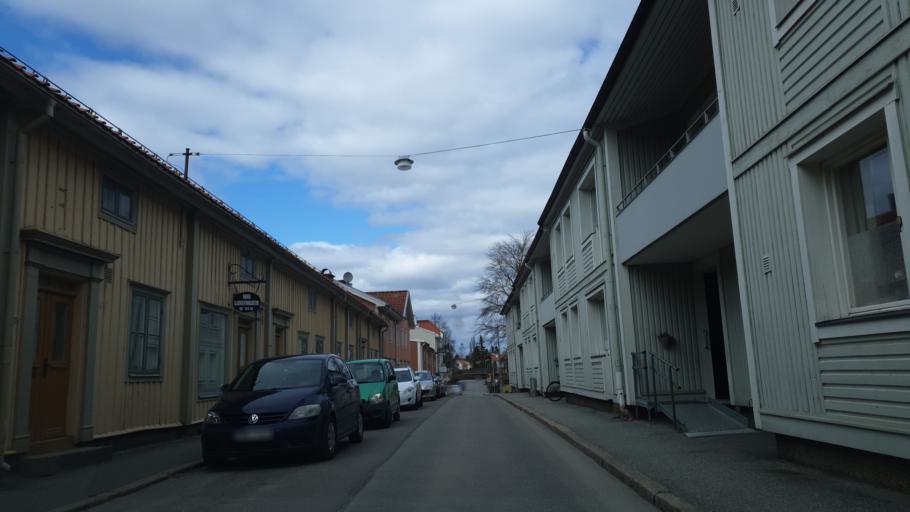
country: SE
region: OErebro
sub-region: Nora Kommun
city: Nora
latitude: 59.5209
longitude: 15.0416
